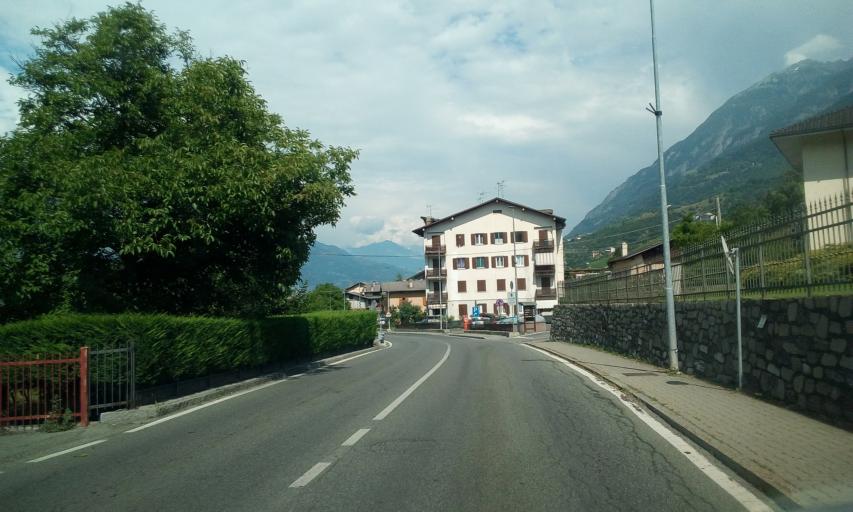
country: IT
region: Aosta Valley
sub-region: Valle d'Aosta
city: Gressan
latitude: 45.7219
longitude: 7.2938
